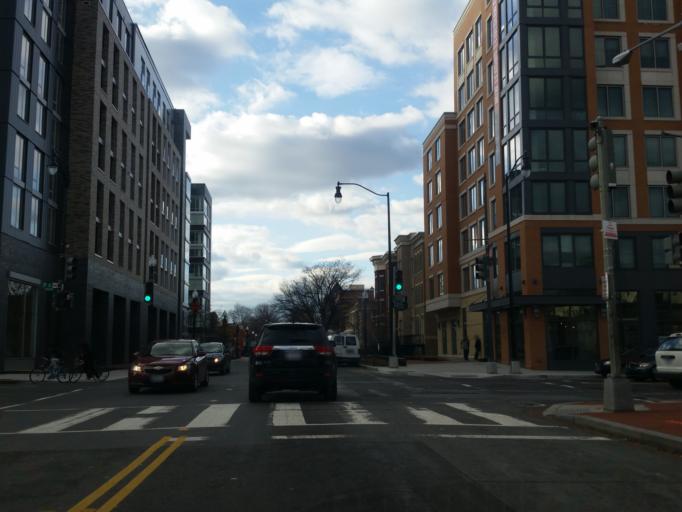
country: US
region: Washington, D.C.
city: Washington, D.C.
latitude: 38.9097
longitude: -77.0217
